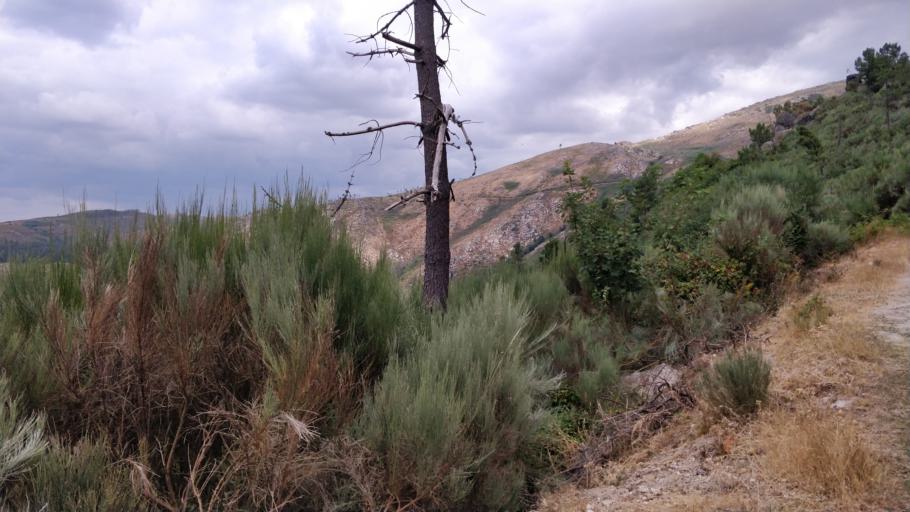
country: PT
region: Guarda
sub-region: Seia
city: Seia
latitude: 40.3774
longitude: -7.6951
